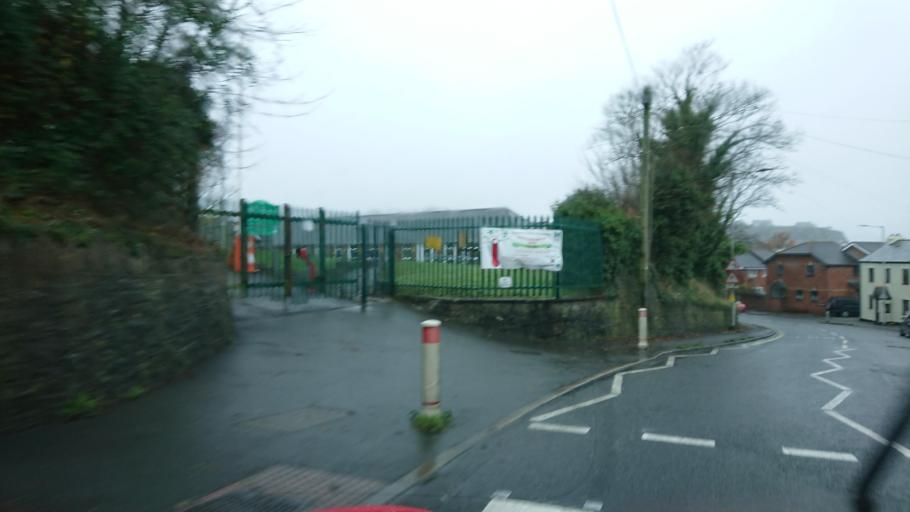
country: GB
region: England
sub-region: Plymouth
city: Plymstock
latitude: 50.3529
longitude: -4.1108
